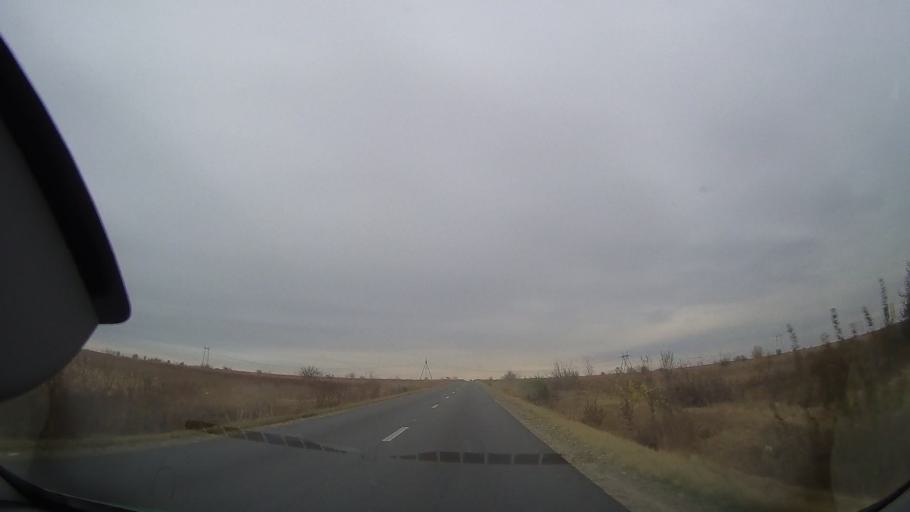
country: RO
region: Ialomita
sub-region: Oras Amara
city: Amara
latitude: 44.6350
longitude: 27.3009
